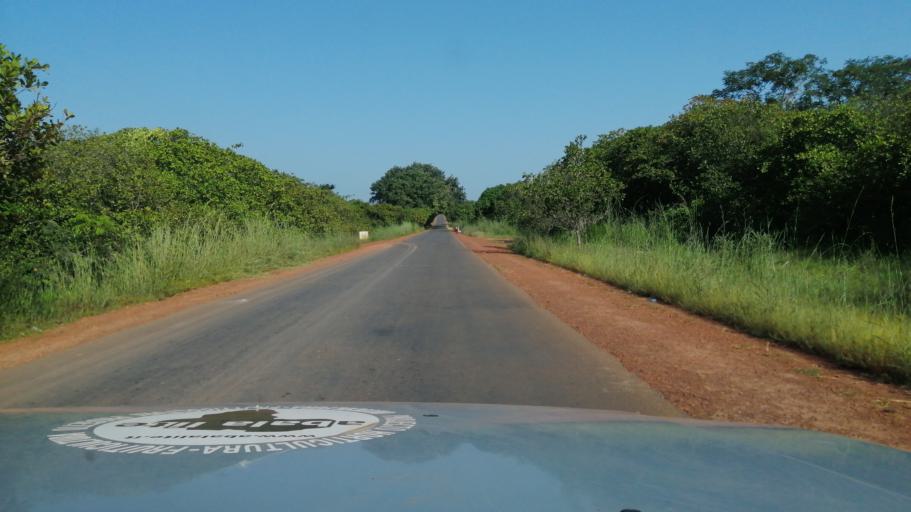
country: GW
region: Bissau
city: Bissau
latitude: 11.9589
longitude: -15.5313
